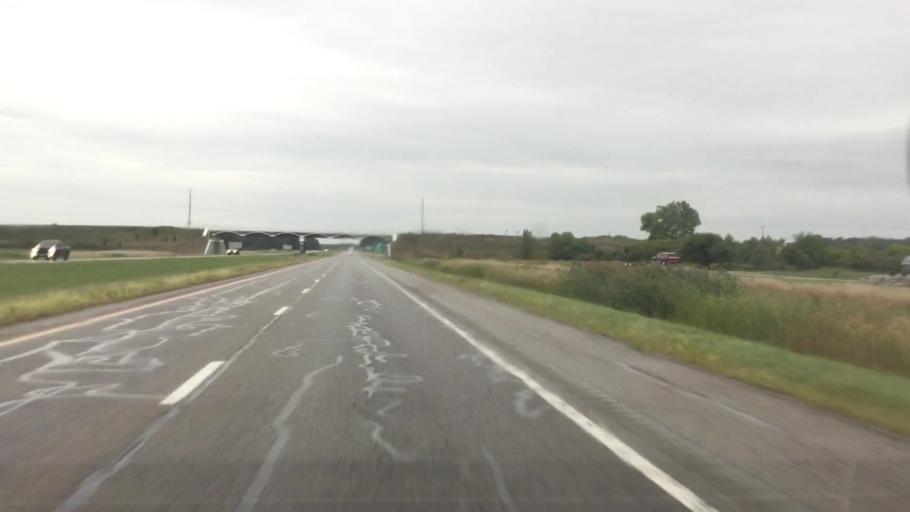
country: US
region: Ohio
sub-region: Defiance County
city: Defiance
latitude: 41.3086
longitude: -84.3378
